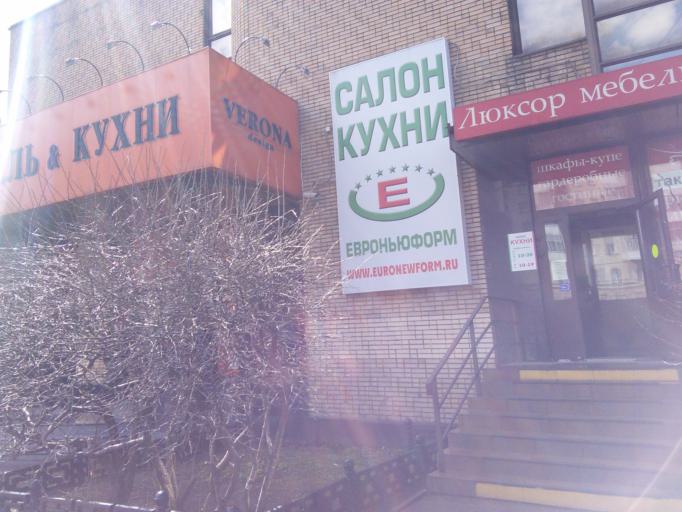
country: RU
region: Moscow
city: Taganskiy
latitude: 55.7362
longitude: 37.6553
